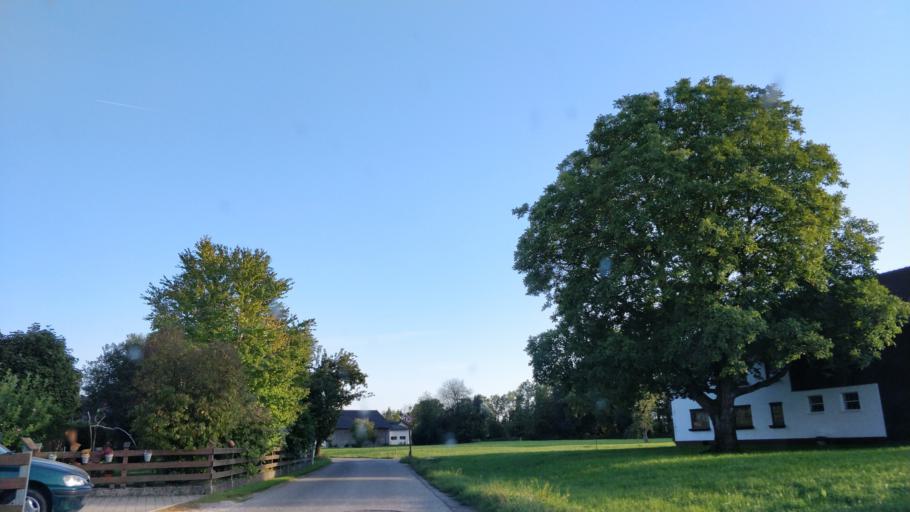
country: AT
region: Upper Austria
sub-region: Politischer Bezirk Braunau am Inn
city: Braunau am Inn
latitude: 48.1657
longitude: 13.1278
